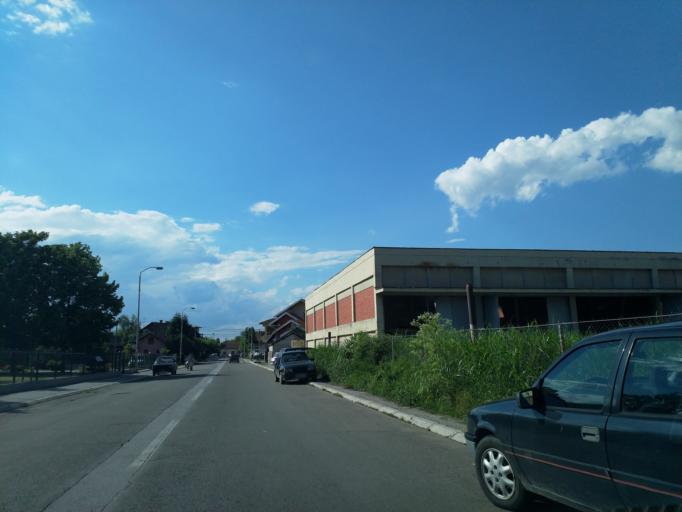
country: RS
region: Central Serbia
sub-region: Pomoravski Okrug
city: Paracin
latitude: 43.8596
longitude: 21.4045
